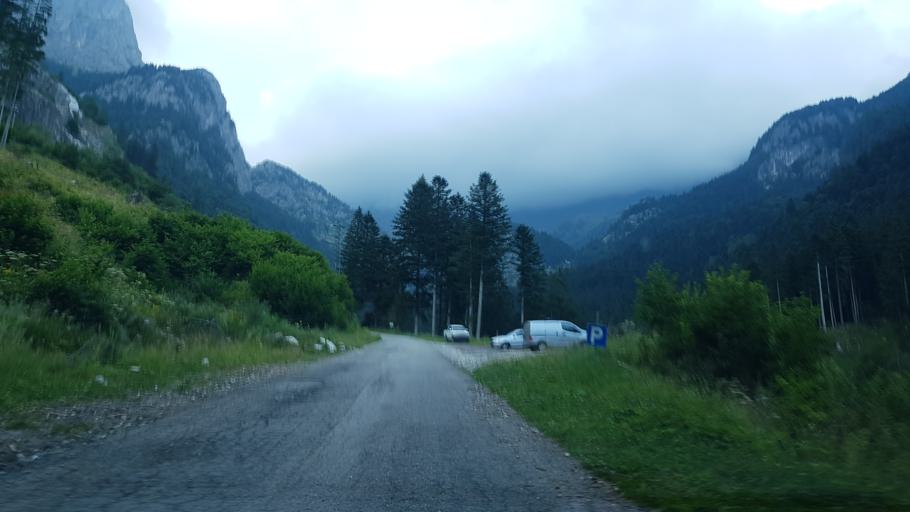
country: IT
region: Friuli Venezia Giulia
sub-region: Provincia di Udine
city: Forni Avoltri
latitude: 46.6126
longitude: 12.7787
